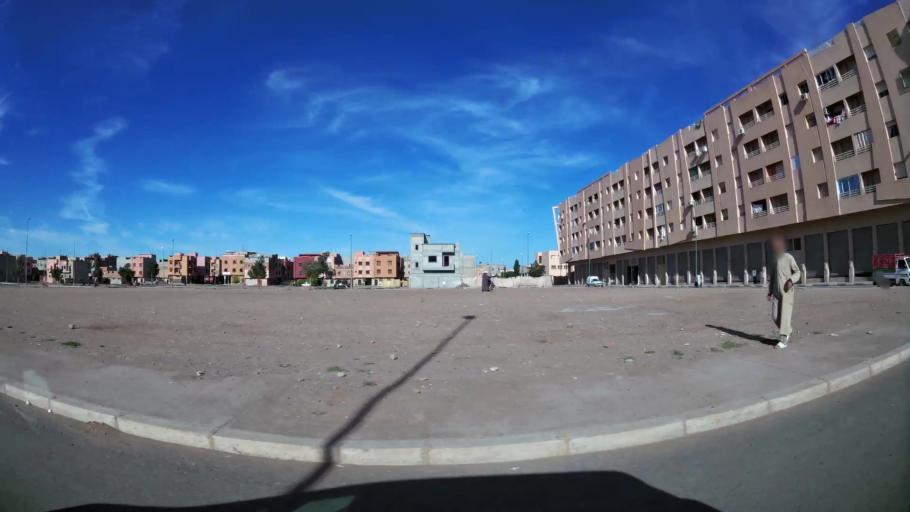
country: MA
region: Marrakech-Tensift-Al Haouz
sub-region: Marrakech
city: Marrakesh
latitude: 31.6871
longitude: -8.0655
